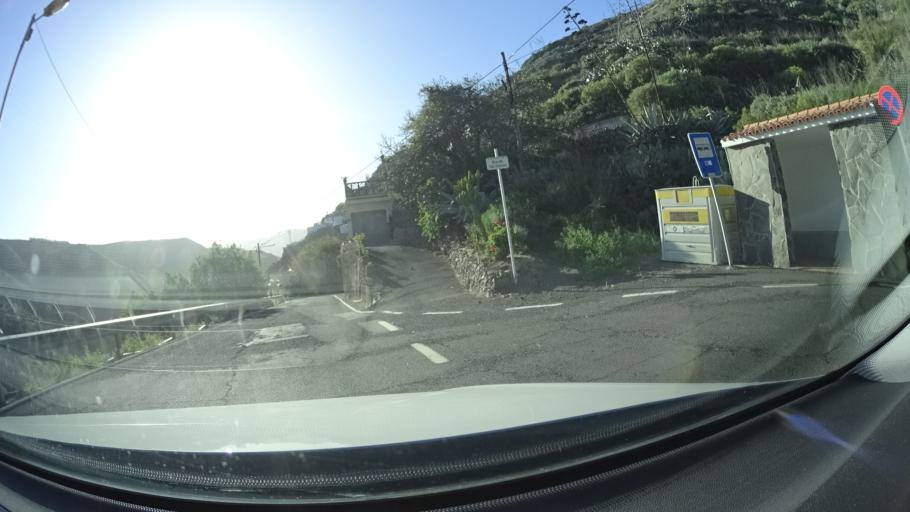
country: ES
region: Canary Islands
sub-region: Provincia de Las Palmas
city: Artenara
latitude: 28.0438
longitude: -15.6485
